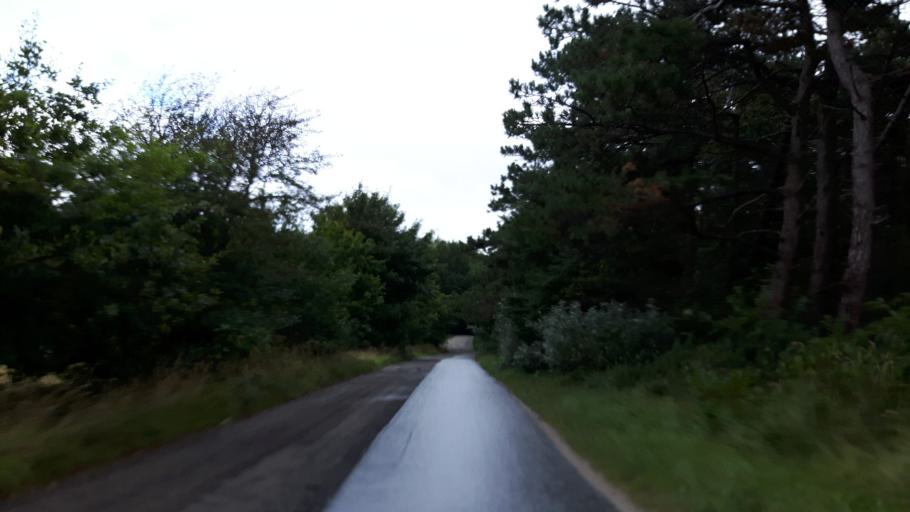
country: NL
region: Friesland
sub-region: Gemeente Ameland
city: Nes
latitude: 53.4522
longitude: 5.7569
